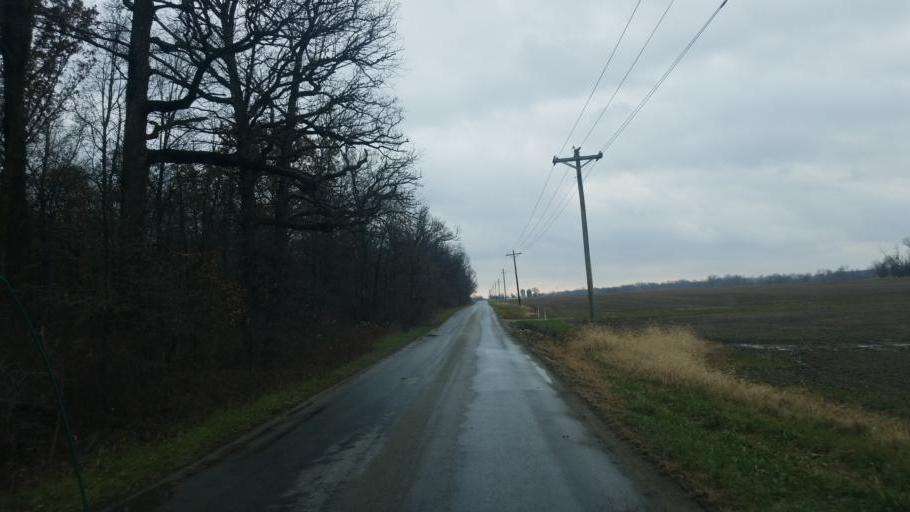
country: US
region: Indiana
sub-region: Adams County
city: Geneva
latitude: 40.5546
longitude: -84.9918
